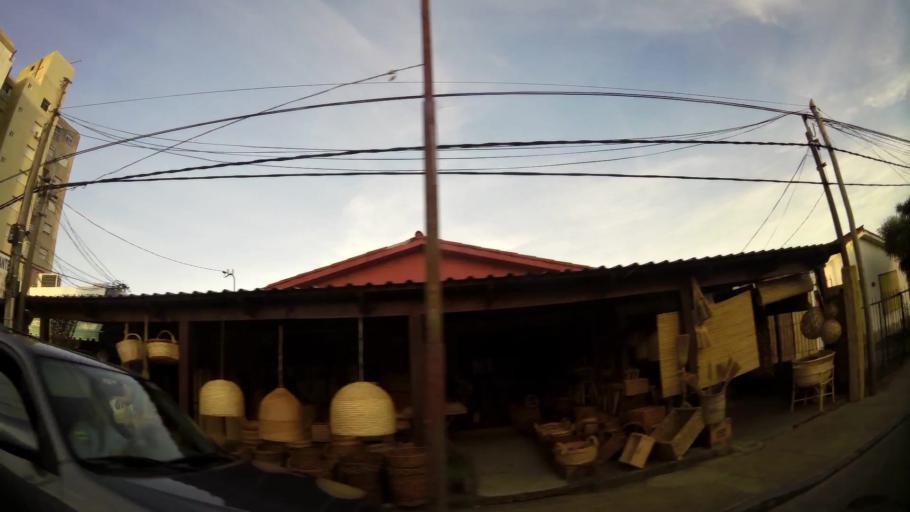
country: UY
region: Maldonado
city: Maldonado
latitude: -34.9106
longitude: -54.9532
